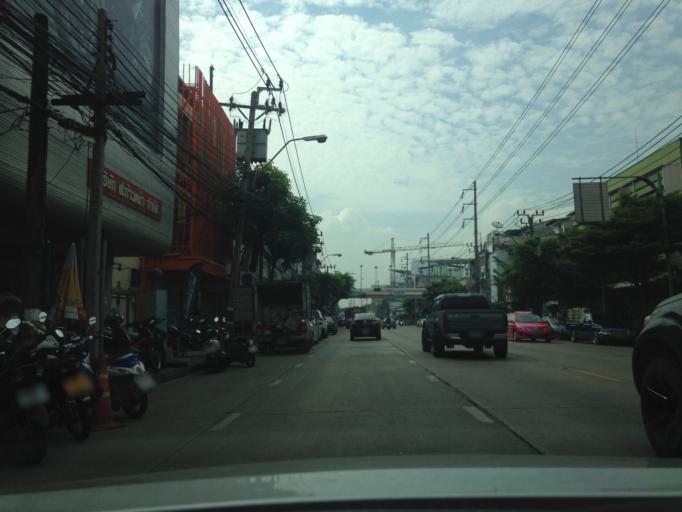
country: TH
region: Bangkok
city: Bang Sue
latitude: 13.8024
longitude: 100.5214
